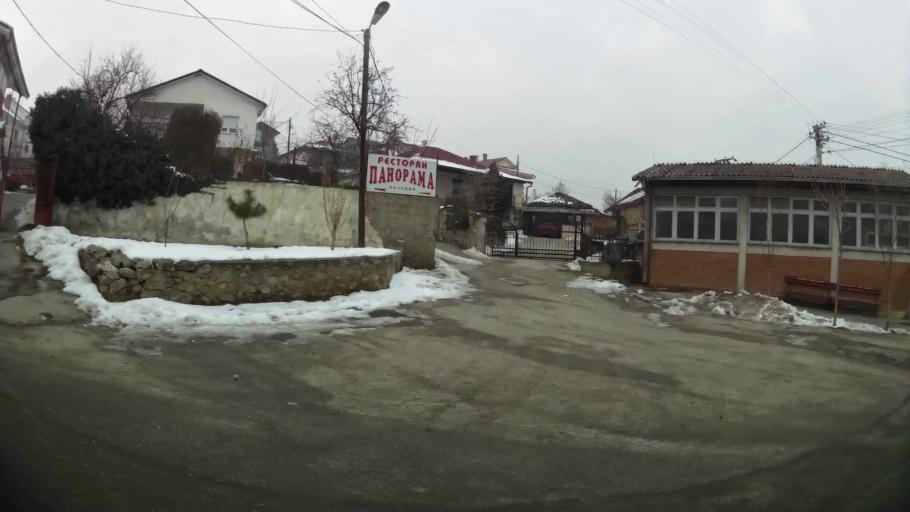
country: MK
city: Kondovo
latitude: 42.0458
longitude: 21.3459
